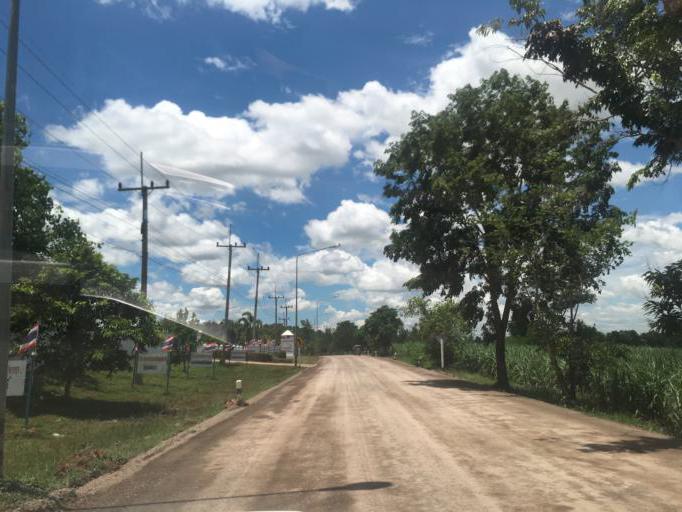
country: TH
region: Changwat Udon Thani
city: Nong Saeng
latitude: 17.1825
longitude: 102.7704
